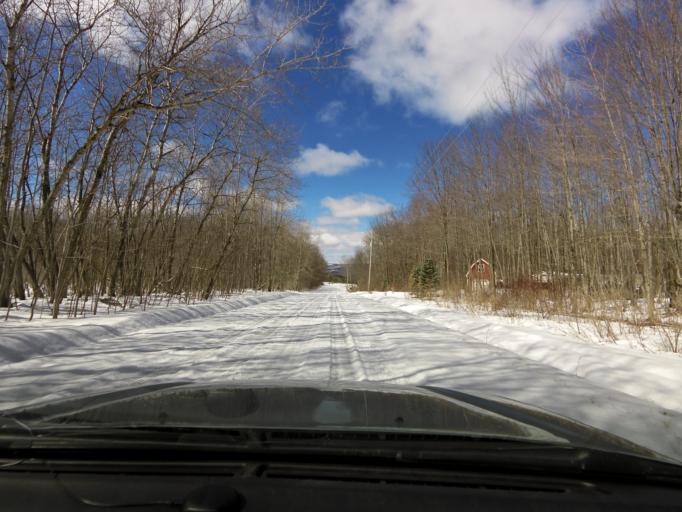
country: US
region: New York
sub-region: Cattaraugus County
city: Franklinville
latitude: 42.3428
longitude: -78.4061
